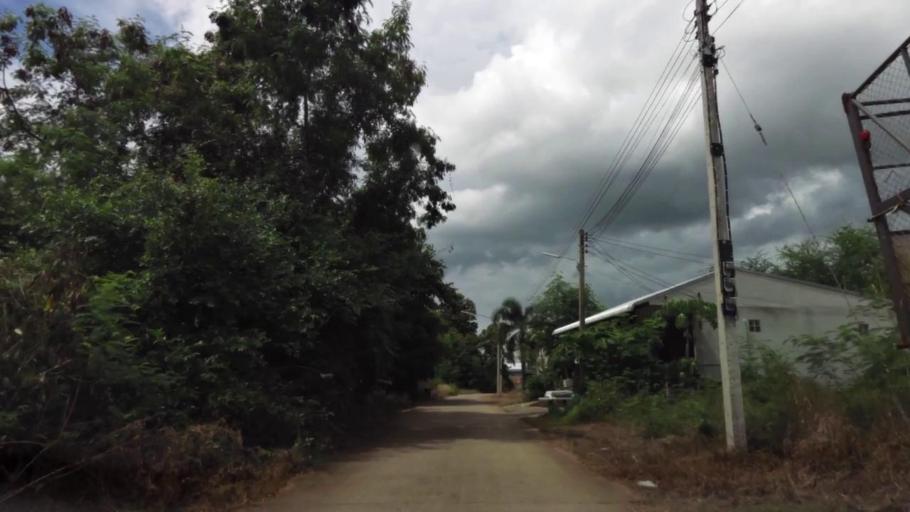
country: TH
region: Nakhon Sawan
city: Phai Sali
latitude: 15.5966
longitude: 100.6492
